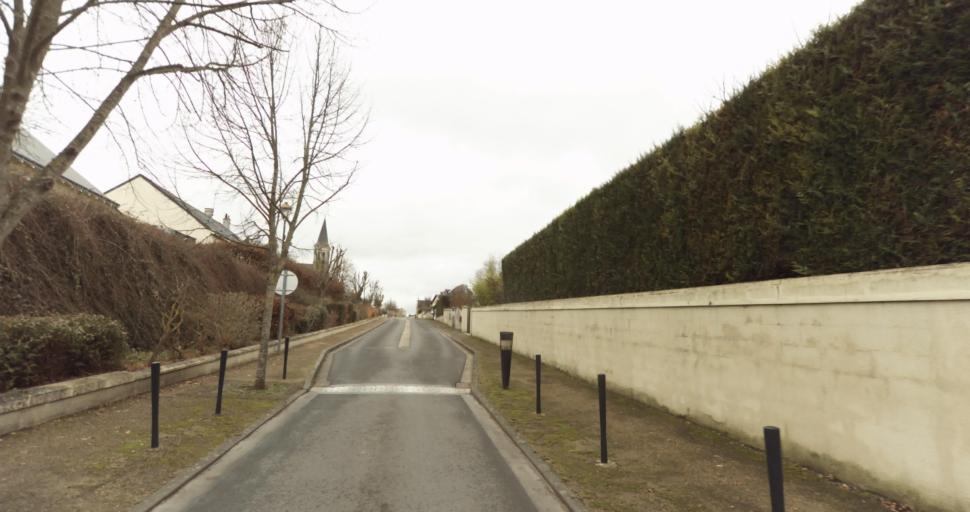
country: FR
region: Pays de la Loire
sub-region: Departement de Maine-et-Loire
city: Chace
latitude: 47.2154
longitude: -0.0782
